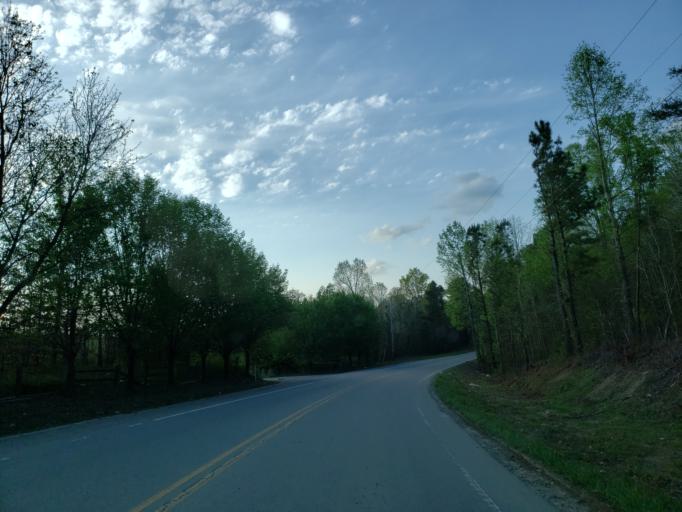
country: US
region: Georgia
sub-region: Cherokee County
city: Ball Ground
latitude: 34.2885
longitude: -84.3852
